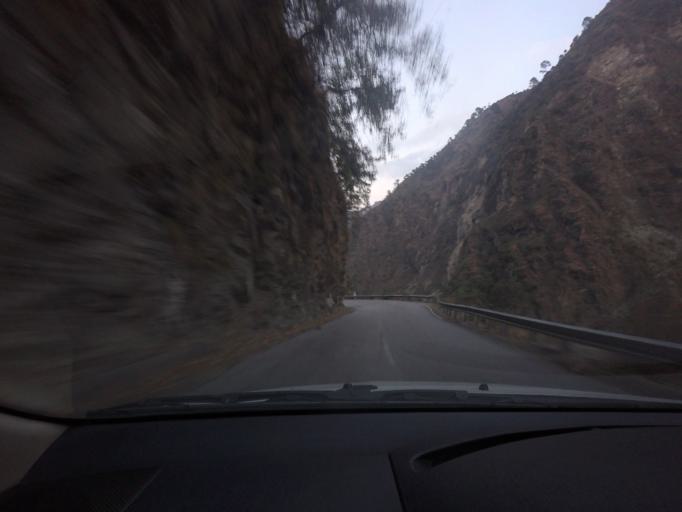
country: IN
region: Himachal Pradesh
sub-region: Mandi
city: Pandoh
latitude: 31.6869
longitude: 77.1090
